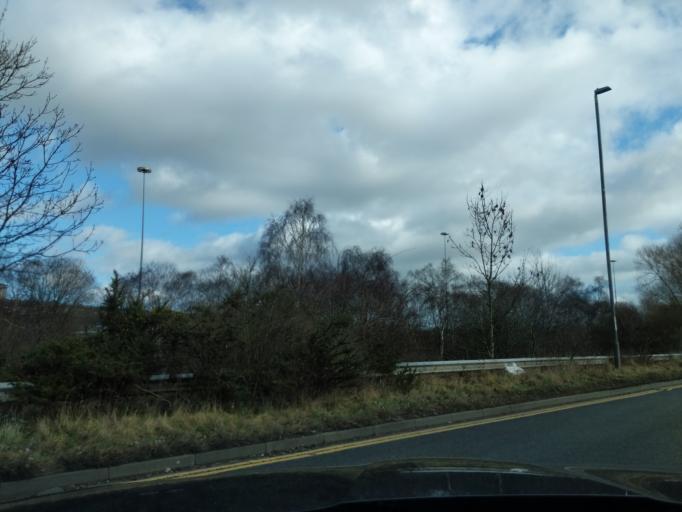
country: GB
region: England
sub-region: Newcastle upon Tyne
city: Benwell
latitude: 54.9607
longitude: -1.6721
